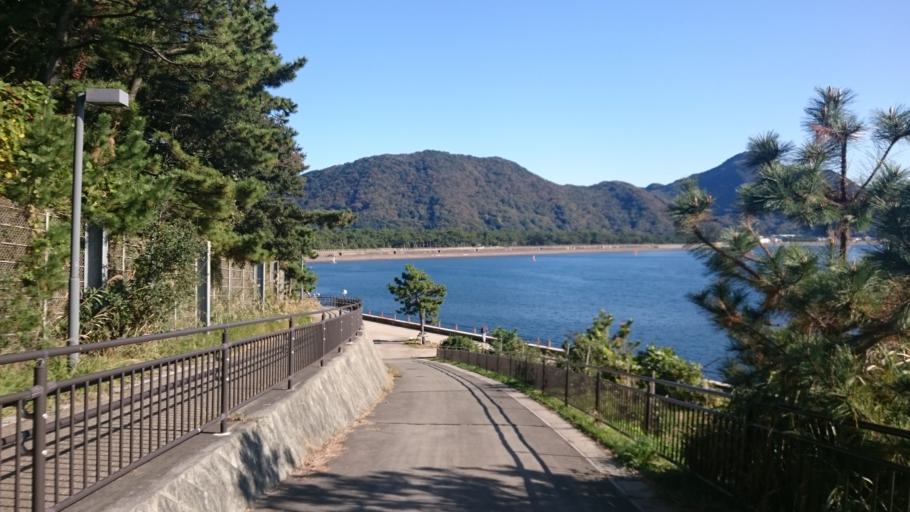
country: JP
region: Shizuoka
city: Numazu
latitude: 35.0727
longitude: 138.8638
